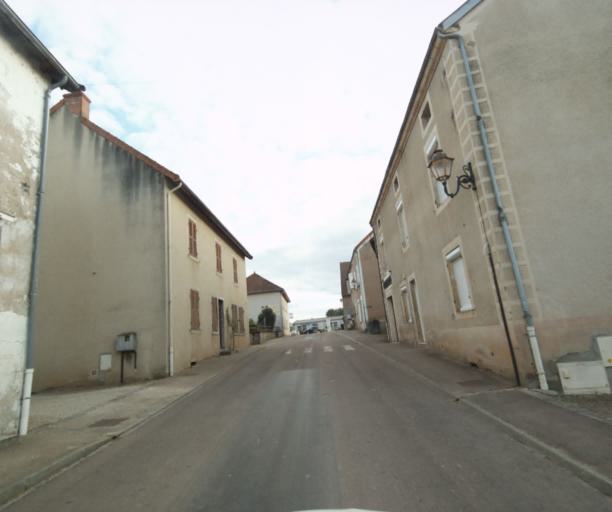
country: FR
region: Bourgogne
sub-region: Departement de Saone-et-Loire
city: Charolles
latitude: 46.4420
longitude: 4.3377
